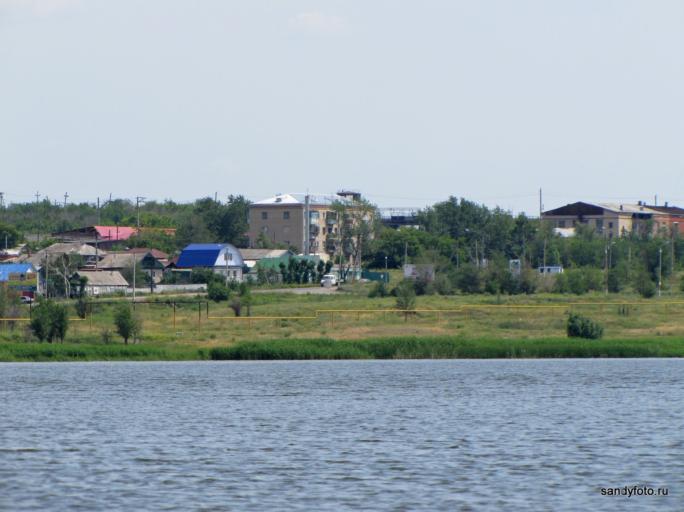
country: RU
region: Chelyabinsk
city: Troitsk
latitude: 54.0894
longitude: 61.5824
